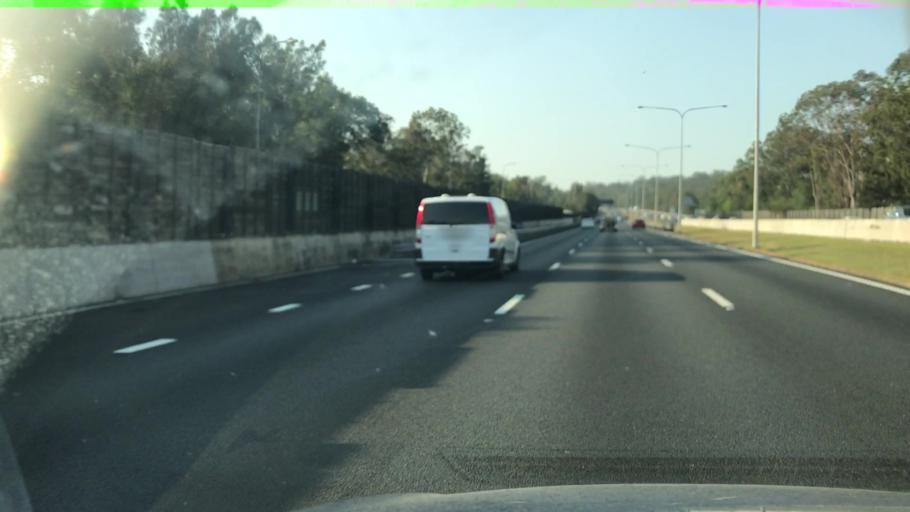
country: AU
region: Queensland
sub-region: Brisbane
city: Tarragindi
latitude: -27.5328
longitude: 153.0579
